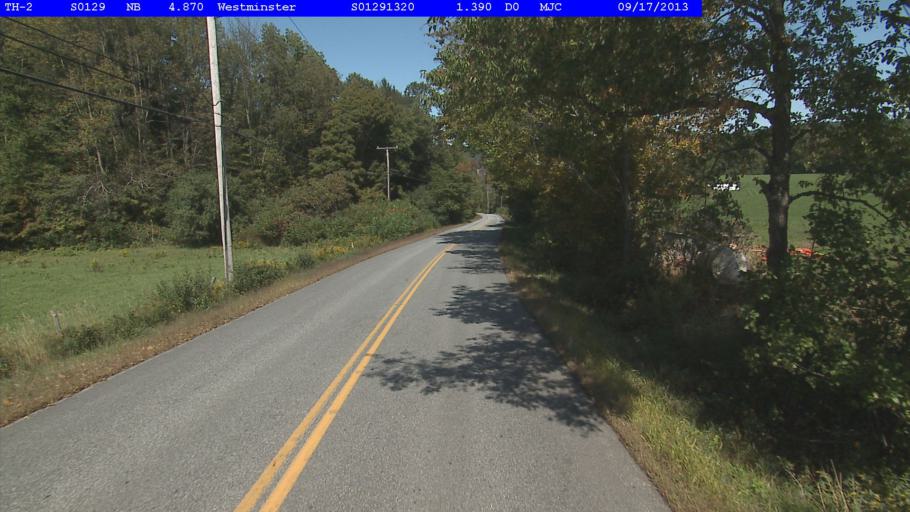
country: US
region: New Hampshire
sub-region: Cheshire County
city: Westmoreland
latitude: 43.0407
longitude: -72.5262
